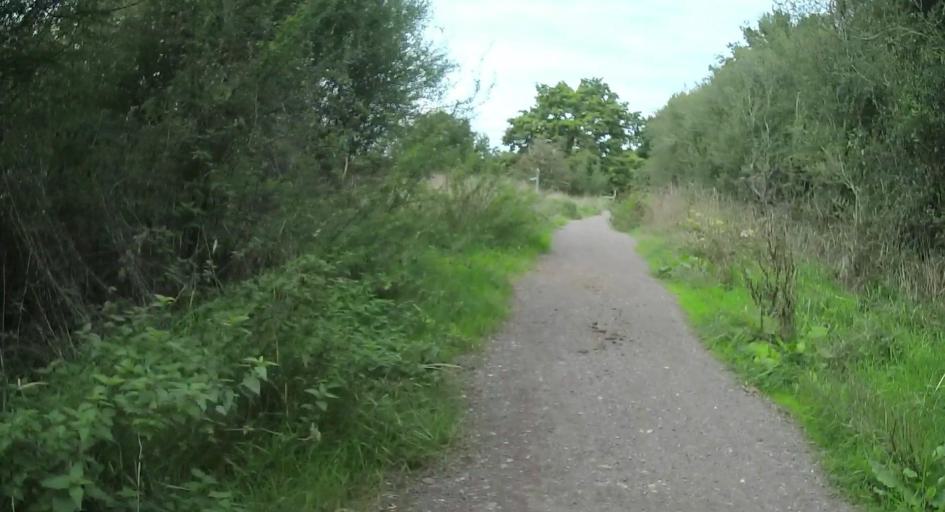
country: GB
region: England
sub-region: Surrey
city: Woking
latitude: 51.3443
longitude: -0.5637
